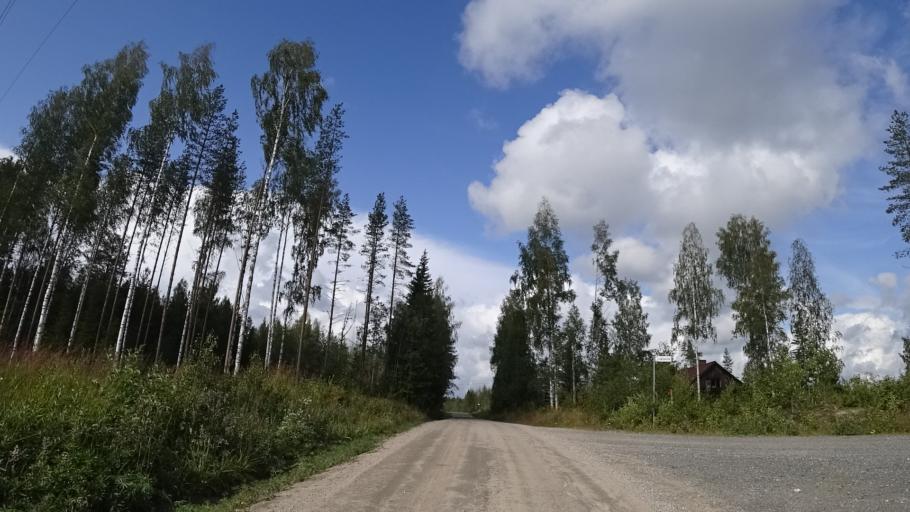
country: FI
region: North Karelia
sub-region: Pielisen Karjala
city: Lieksa
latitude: 63.5870
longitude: 30.1346
